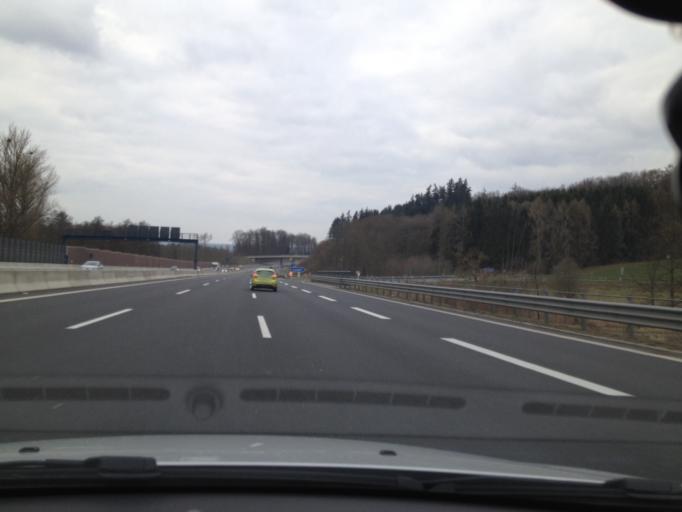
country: DE
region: Bavaria
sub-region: Regierungsbezirk Unterfranken
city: Sailauf
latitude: 49.9836
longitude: 9.2621
